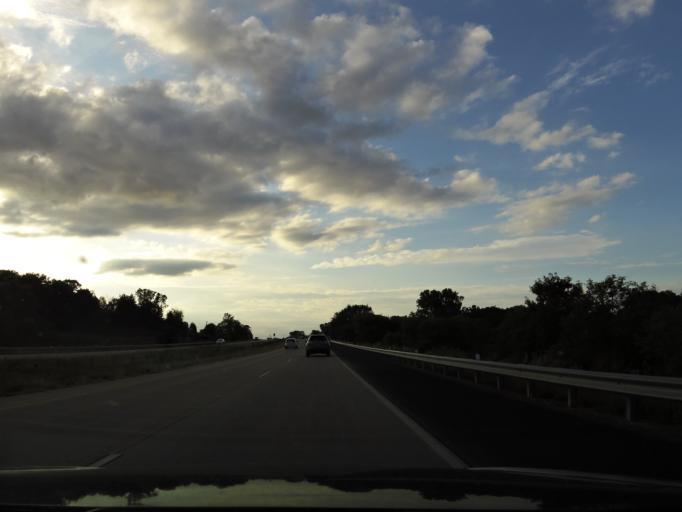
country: US
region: Minnesota
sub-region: Washington County
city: Cottage Grove
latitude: 44.7998
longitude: -92.9015
